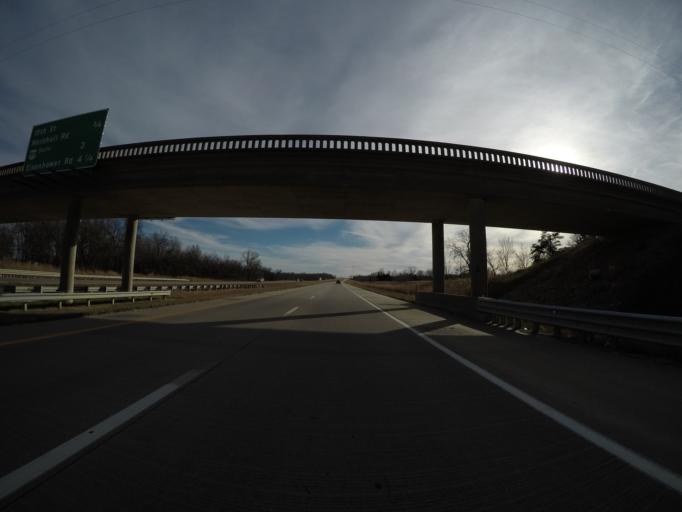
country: US
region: Kansas
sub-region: Franklin County
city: Ottawa
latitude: 38.6086
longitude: -95.2327
